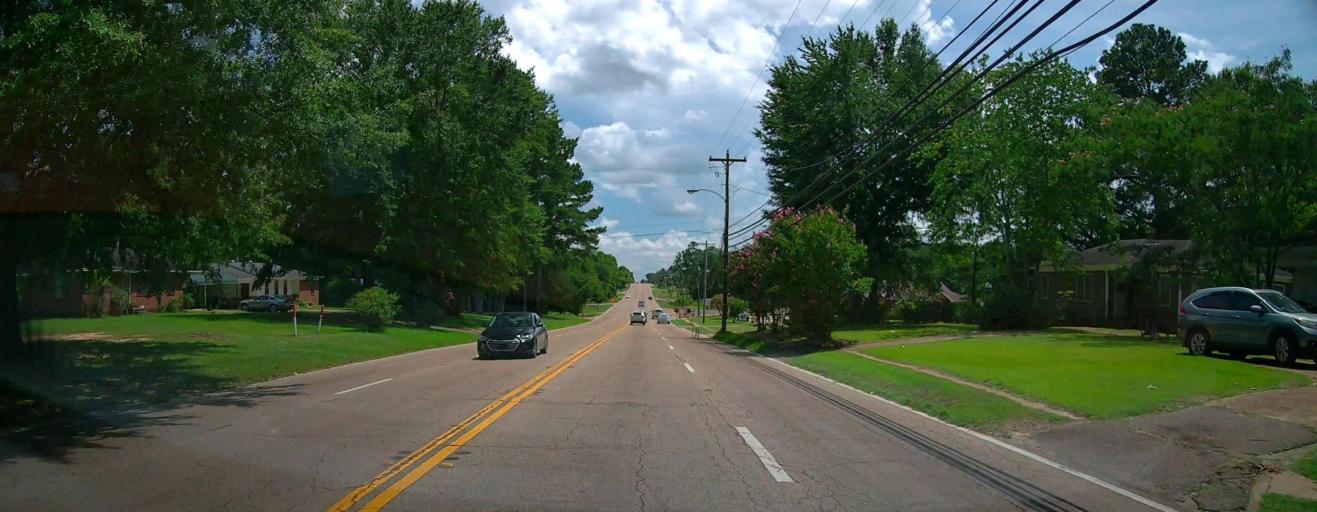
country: US
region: Mississippi
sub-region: Lee County
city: Verona
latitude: 34.1896
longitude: -88.7199
